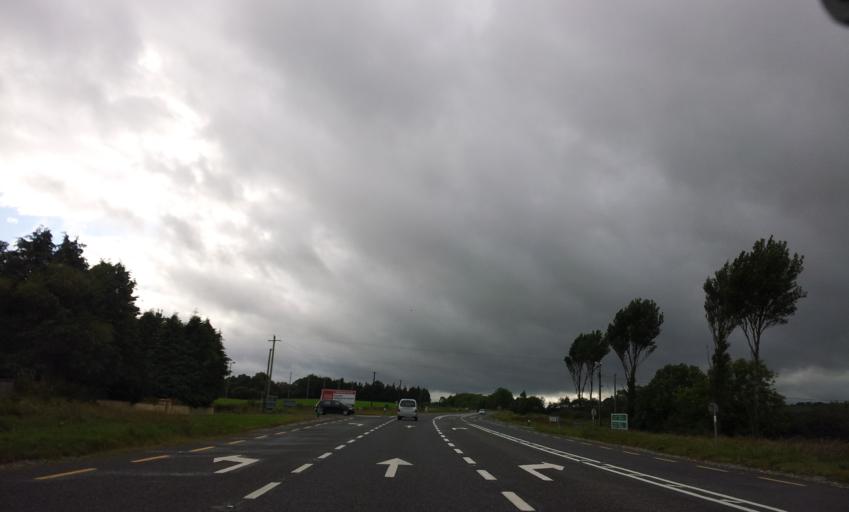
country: IE
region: Munster
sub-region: County Cork
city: Youghal
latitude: 51.9390
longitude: -7.9255
